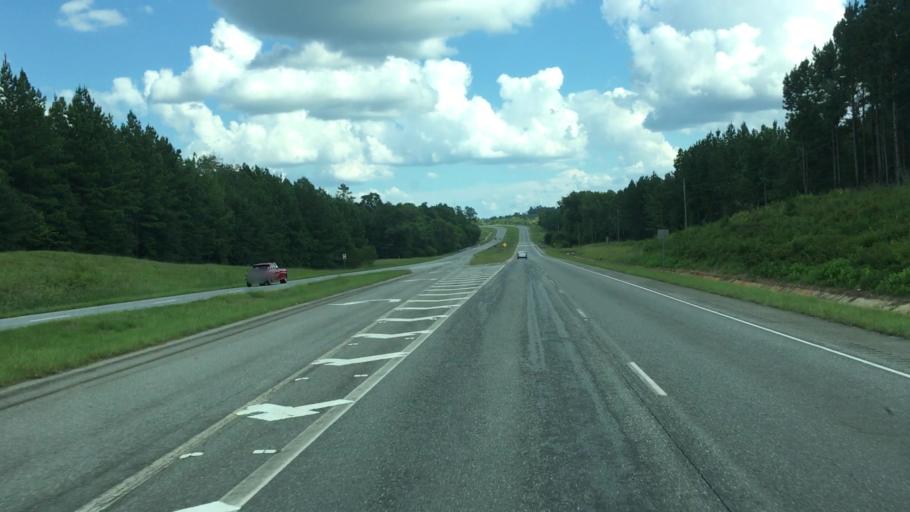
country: US
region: Georgia
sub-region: Wilkinson County
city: Irwinton
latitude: 32.7023
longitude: -83.1249
